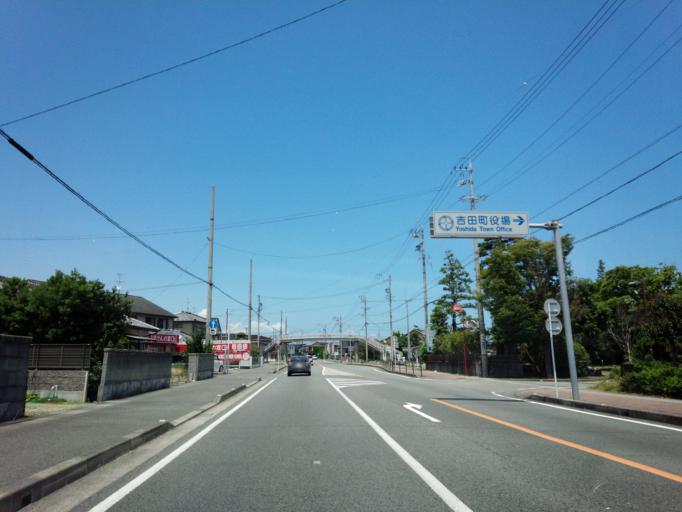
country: JP
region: Shizuoka
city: Shimada
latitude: 34.7707
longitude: 138.2508
